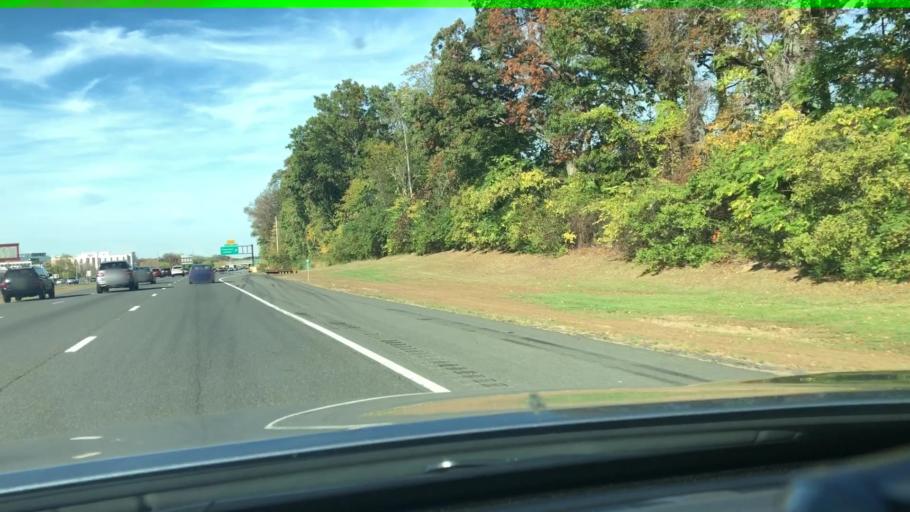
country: US
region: New Jersey
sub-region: Bergen County
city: Paramus
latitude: 40.9554
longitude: -74.0658
